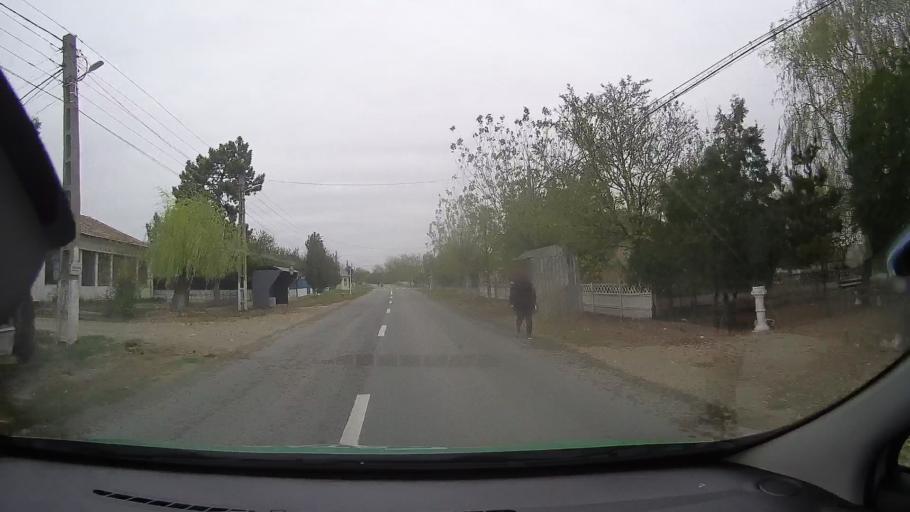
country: RO
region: Constanta
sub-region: Comuna Silistea
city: Silistea
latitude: 44.4451
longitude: 28.2373
